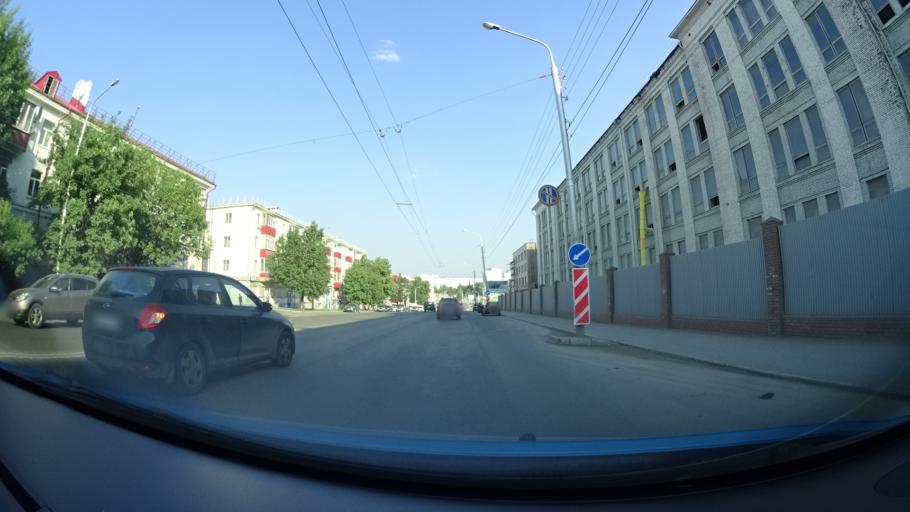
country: RU
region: Bashkortostan
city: Ufa
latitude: 54.7524
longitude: 56.0128
